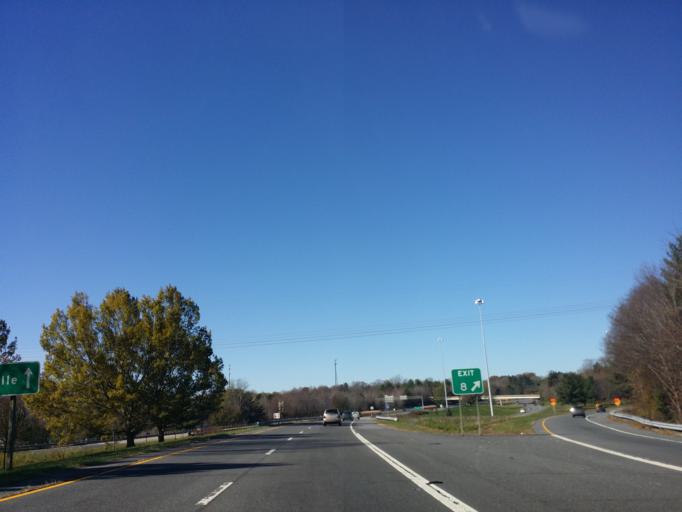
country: US
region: North Carolina
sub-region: Buncombe County
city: Biltmore Forest
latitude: 35.5671
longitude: -82.5006
